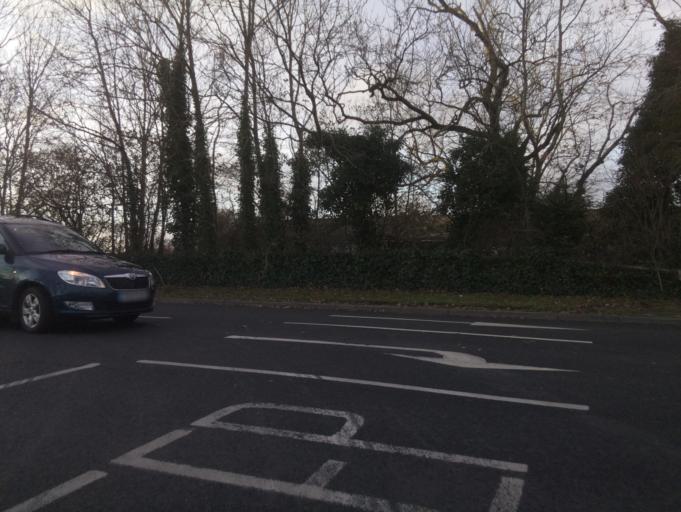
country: GB
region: England
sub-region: Cumbria
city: Scotby
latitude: 54.8965
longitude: -2.8959
